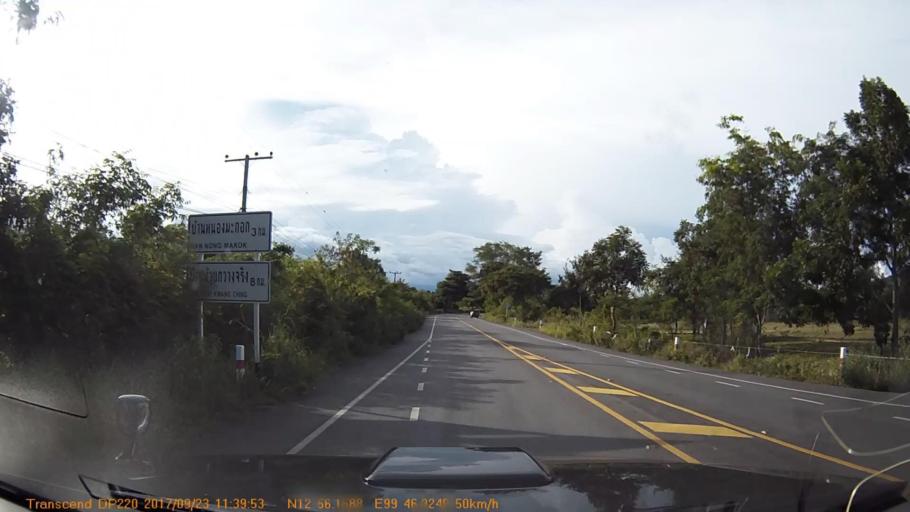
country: TH
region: Phetchaburi
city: Tha Yang
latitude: 12.9361
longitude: 99.7820
